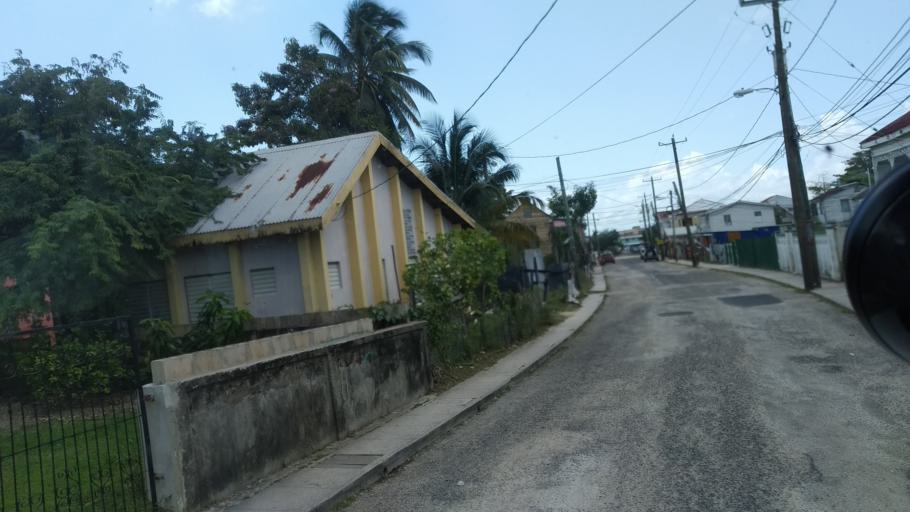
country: BZ
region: Belize
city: Belize City
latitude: 17.4995
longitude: -88.1889
